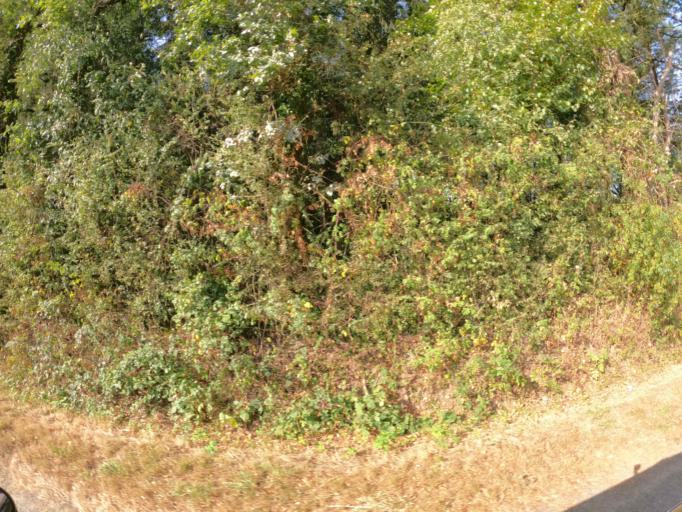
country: FR
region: Pays de la Loire
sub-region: Departement de la Vendee
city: Saint-Christophe-du-Ligneron
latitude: 46.8036
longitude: -1.7977
